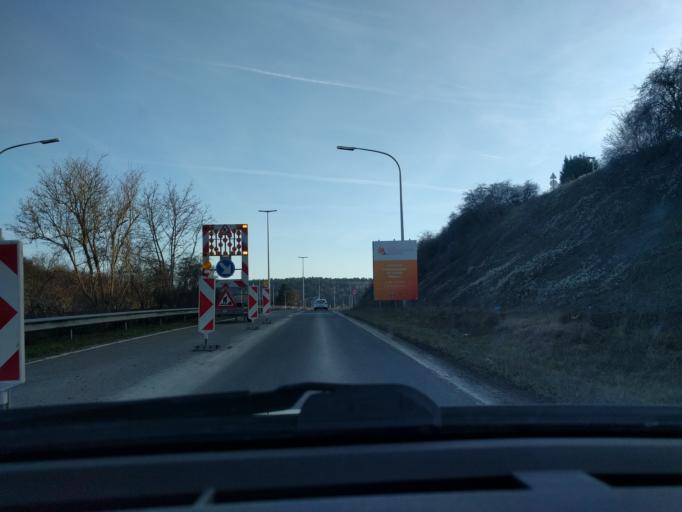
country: BE
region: Wallonia
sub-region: Province de Namur
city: Couvin
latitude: 50.0836
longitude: 4.5134
